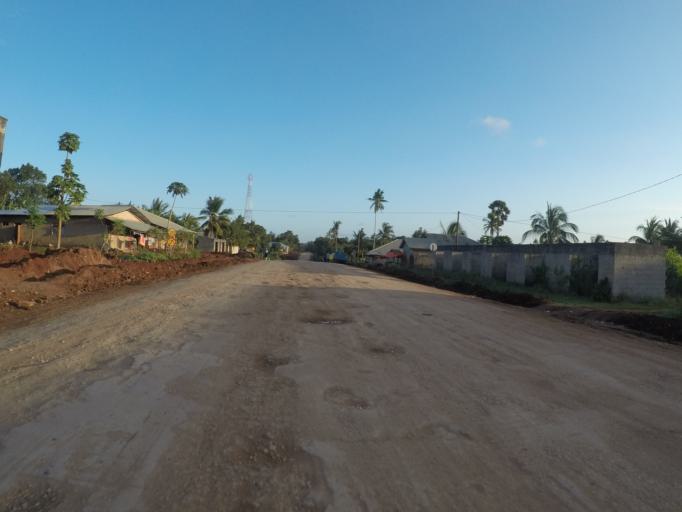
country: TZ
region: Zanzibar North
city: Gamba
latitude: -5.9126
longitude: 39.2991
